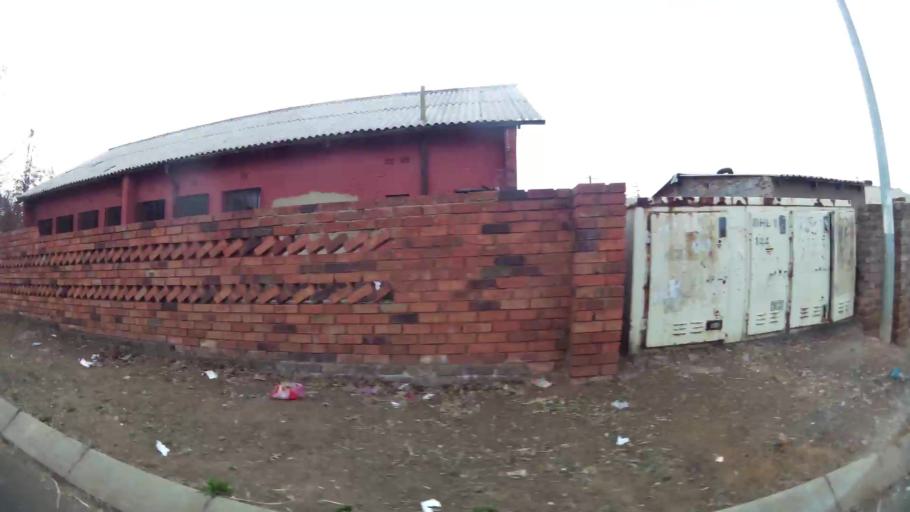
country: ZA
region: Gauteng
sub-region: City of Johannesburg Metropolitan Municipality
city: Soweto
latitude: -26.2707
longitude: 27.8725
